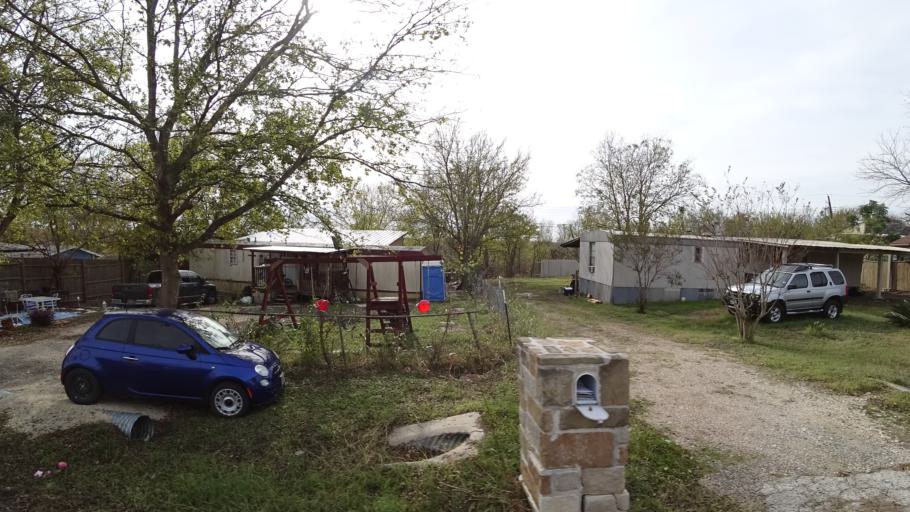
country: US
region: Texas
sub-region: Travis County
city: Garfield
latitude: 30.1293
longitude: -97.6169
